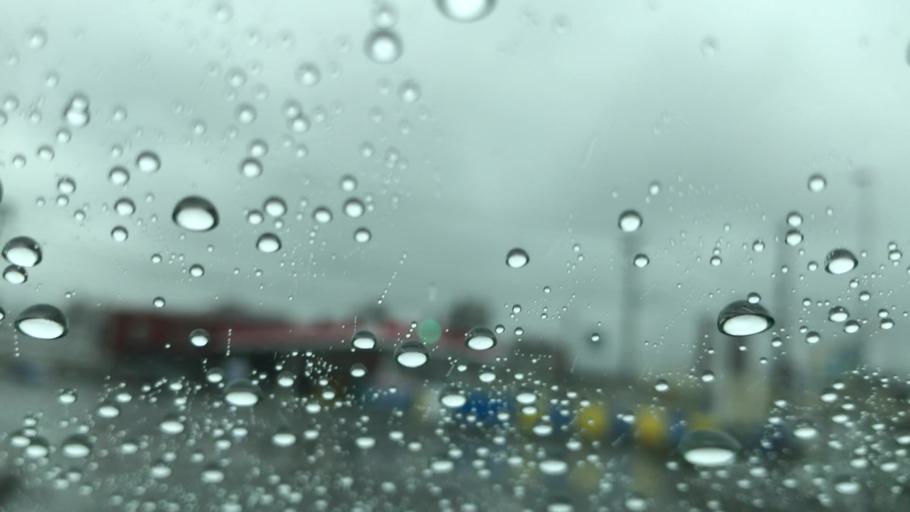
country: JP
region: Hokkaido
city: Otaru
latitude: 43.1876
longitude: 141.0142
